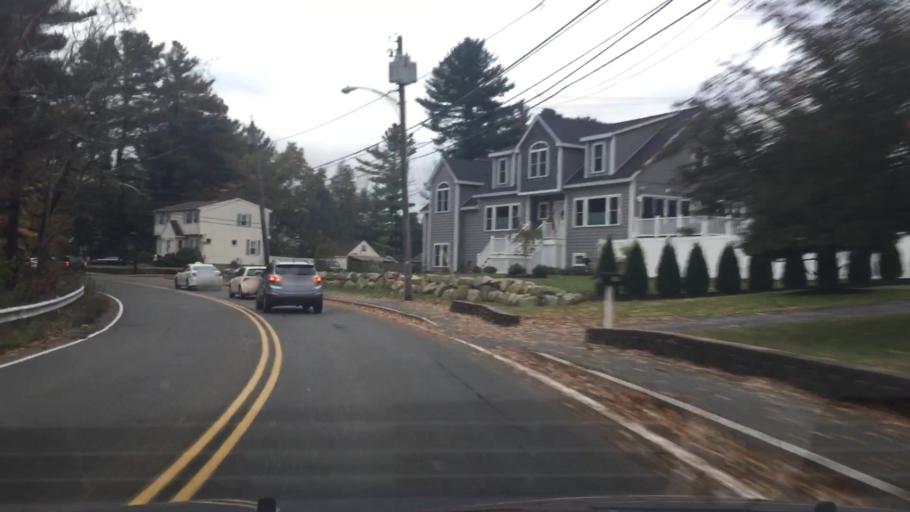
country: US
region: Massachusetts
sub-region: Essex County
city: Saugus
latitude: 42.5029
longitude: -71.0227
